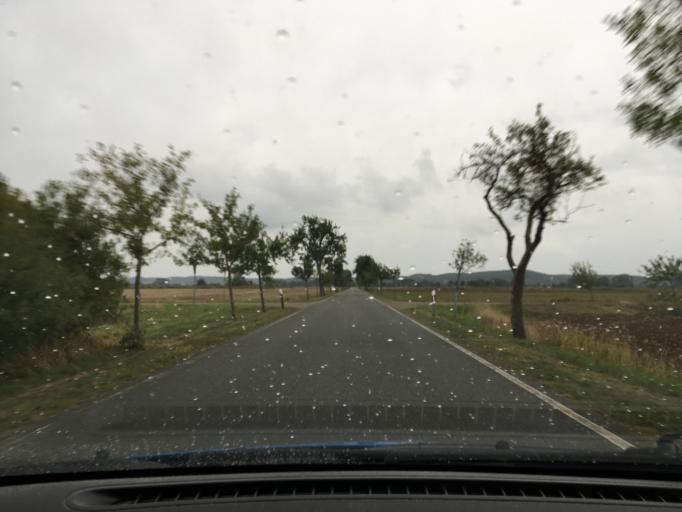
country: DE
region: Lower Saxony
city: Hitzacker
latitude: 53.2194
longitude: 10.9869
